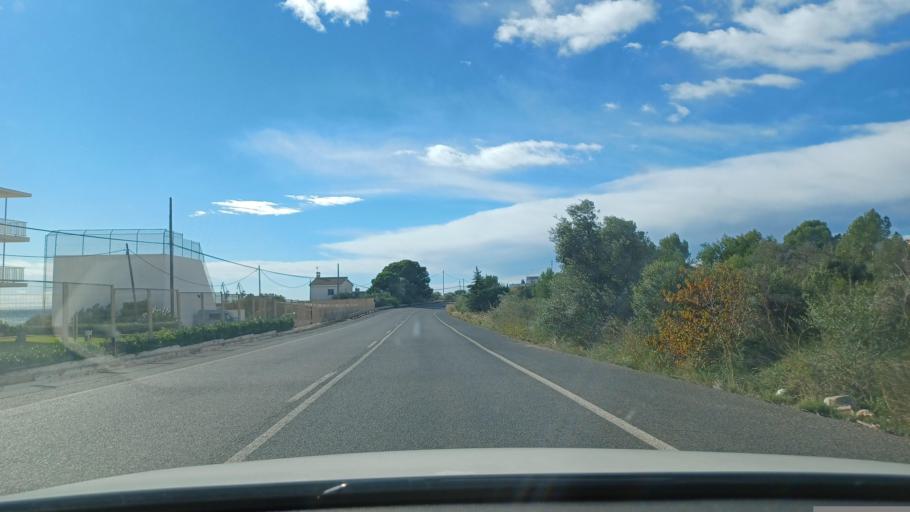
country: ES
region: Catalonia
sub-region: Provincia de Tarragona
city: Sant Carles de la Rapita
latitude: 40.5823
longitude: 0.5556
